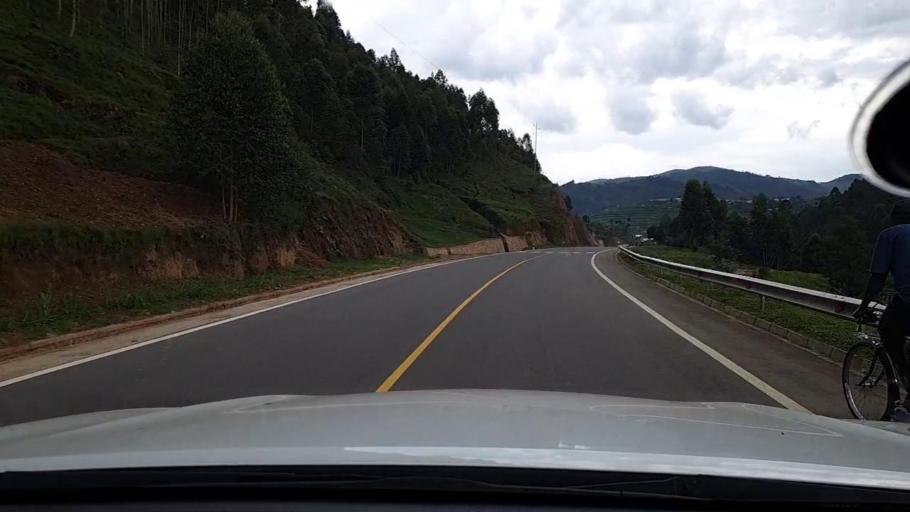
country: RW
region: Northern Province
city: Byumba
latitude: -1.6427
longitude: 29.9253
